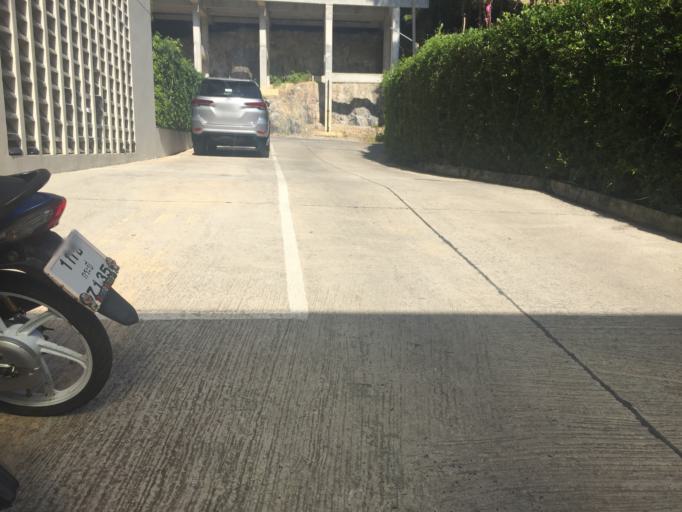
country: TH
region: Phangnga
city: Ban Ao Nang
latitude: 8.0348
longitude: 98.8290
